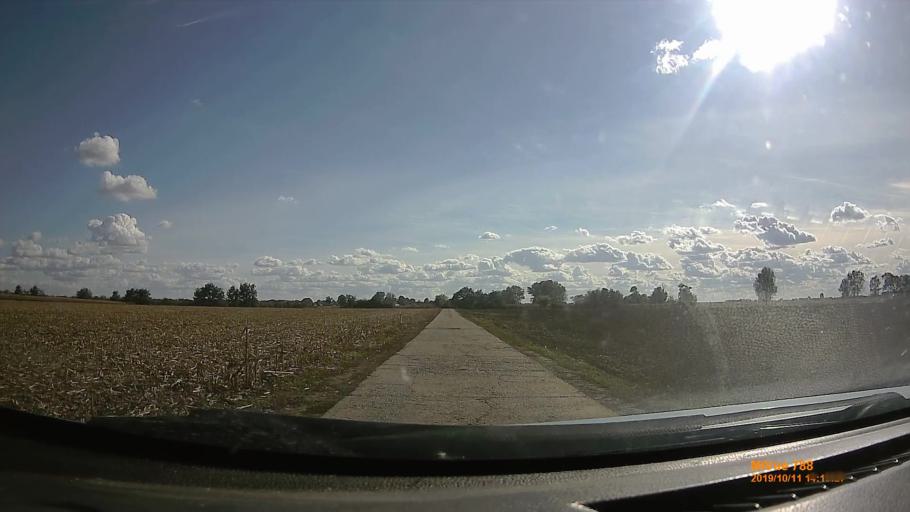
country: HU
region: Hajdu-Bihar
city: Hajduszoboszlo
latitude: 47.5322
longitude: 21.4016
